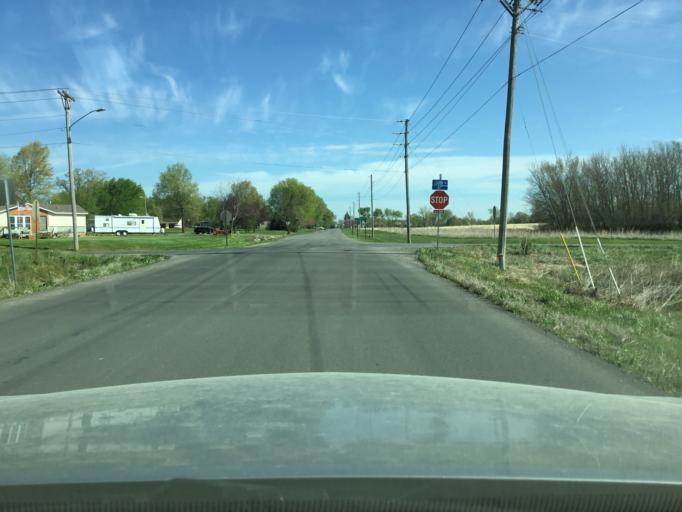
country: US
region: Kansas
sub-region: Neosho County
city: Chanute
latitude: 37.6599
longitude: -95.4435
